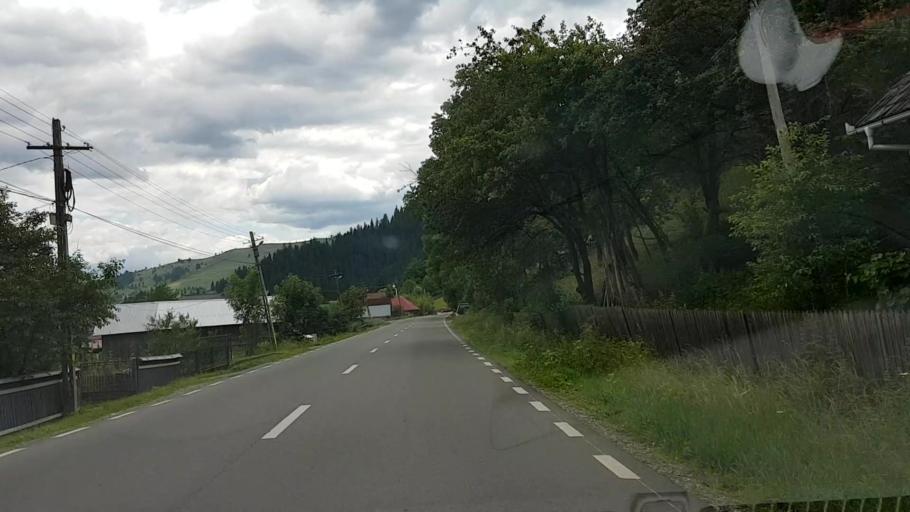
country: RO
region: Neamt
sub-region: Comuna Borca
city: Borca
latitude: 47.1877
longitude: 25.7737
